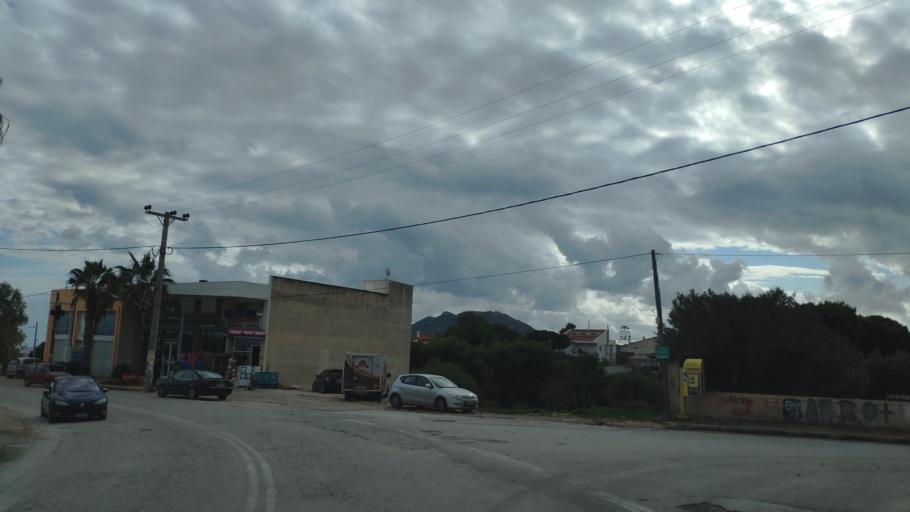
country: GR
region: Attica
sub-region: Nomarchia Anatolikis Attikis
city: Artemida
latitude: 37.9416
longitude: 24.0083
